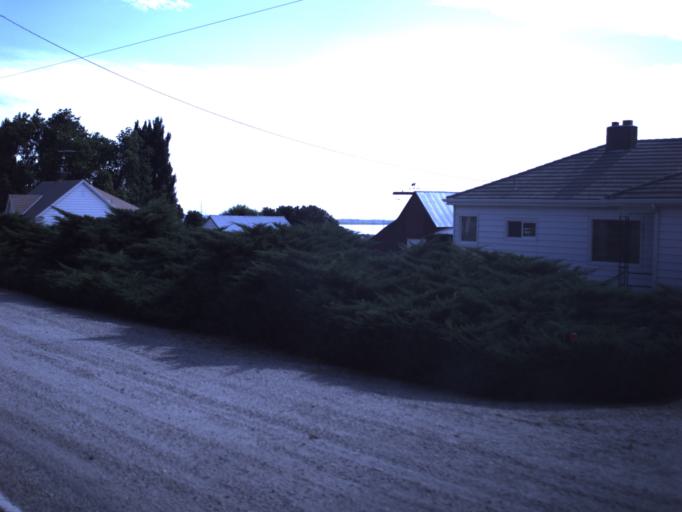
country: US
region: Utah
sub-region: Box Elder County
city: Willard
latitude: 41.4032
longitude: -112.0360
